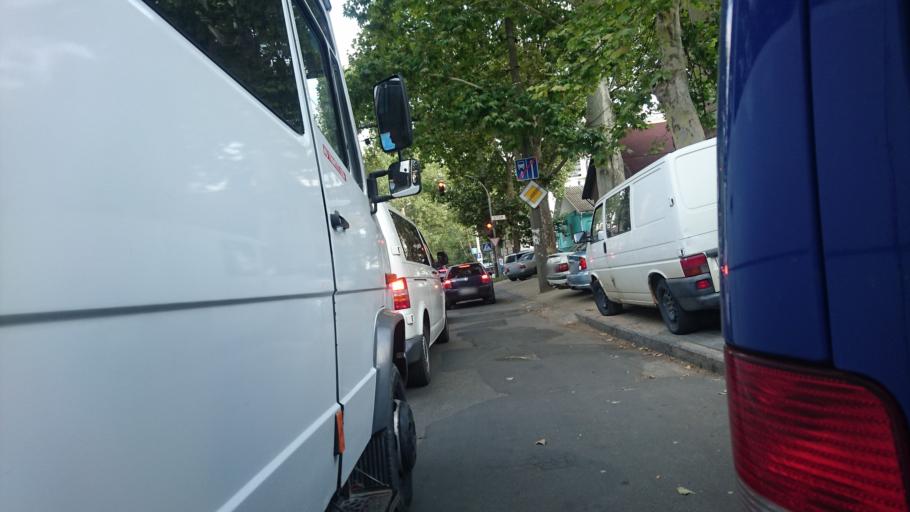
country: MD
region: Chisinau
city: Chisinau
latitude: 47.0142
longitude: 28.8420
